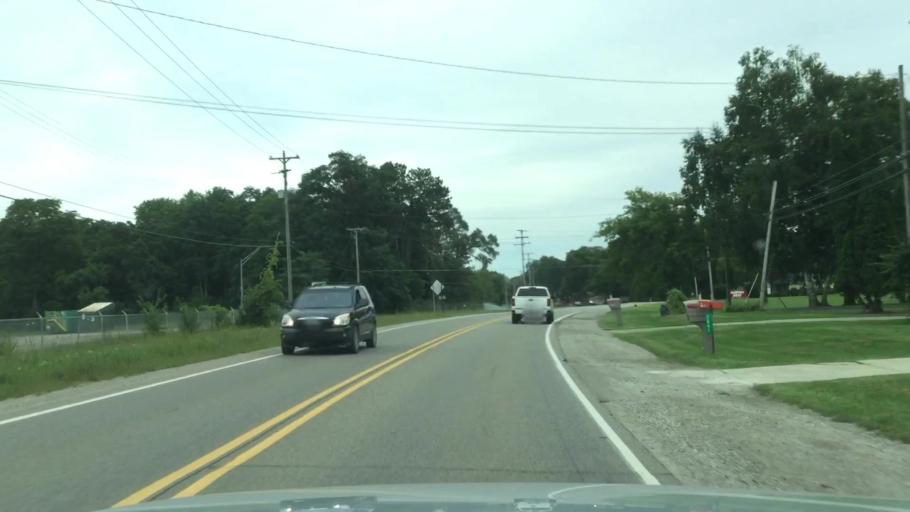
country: US
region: Michigan
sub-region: Genesee County
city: Linden
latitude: 42.8109
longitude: -83.8081
